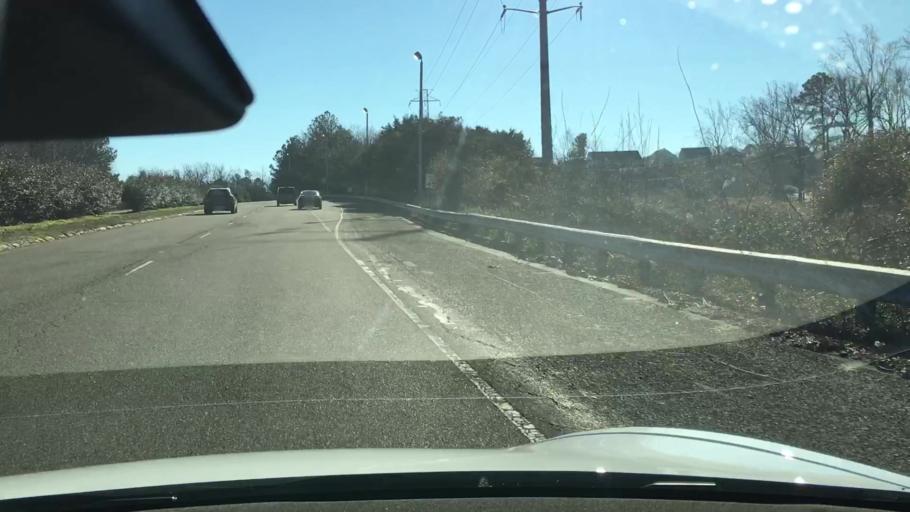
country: US
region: Virginia
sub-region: Chesterfield County
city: Bon Air
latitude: 37.5458
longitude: -77.5589
